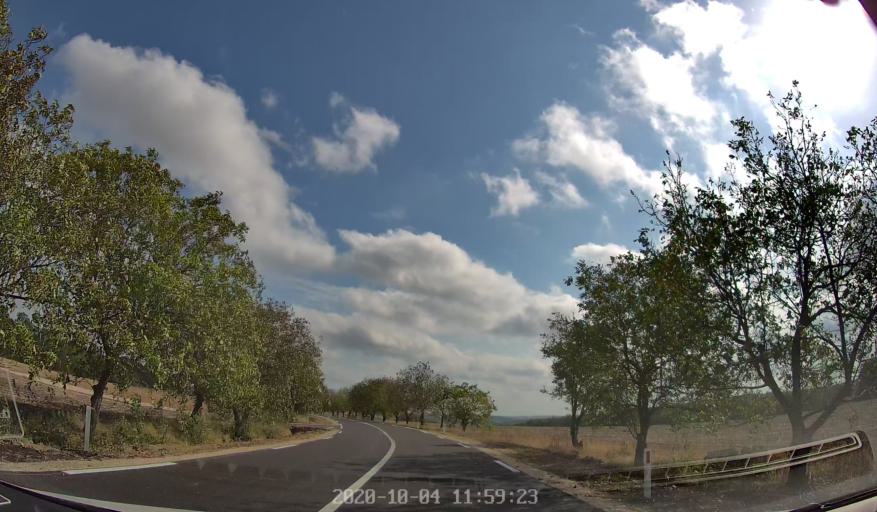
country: MD
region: Rezina
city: Saharna
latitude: 47.6319
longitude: 28.8502
